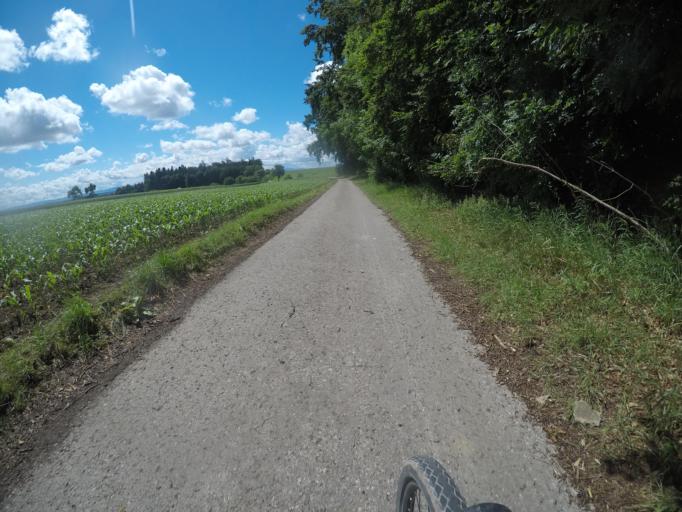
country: DE
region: Baden-Wuerttemberg
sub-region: Regierungsbezirk Stuttgart
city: Motzingen
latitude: 48.5036
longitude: 8.7477
